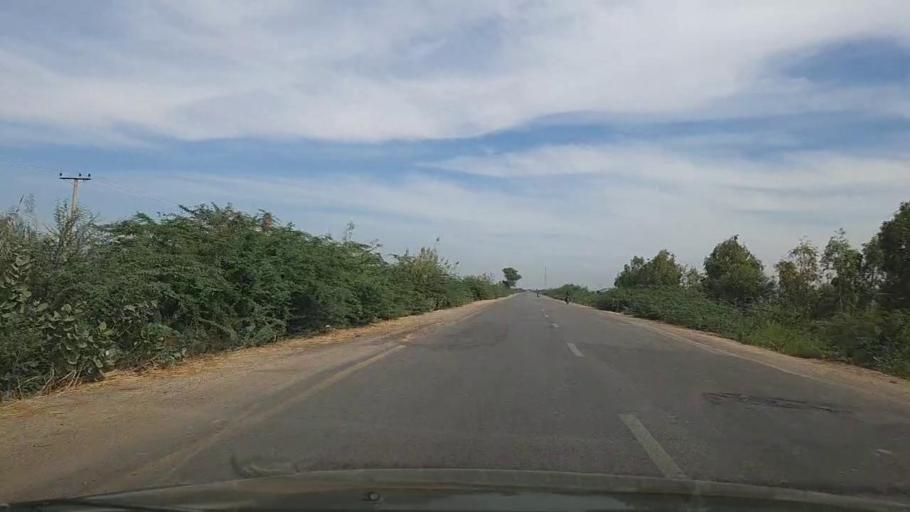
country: PK
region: Sindh
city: Thatta
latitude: 24.8024
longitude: 67.9672
